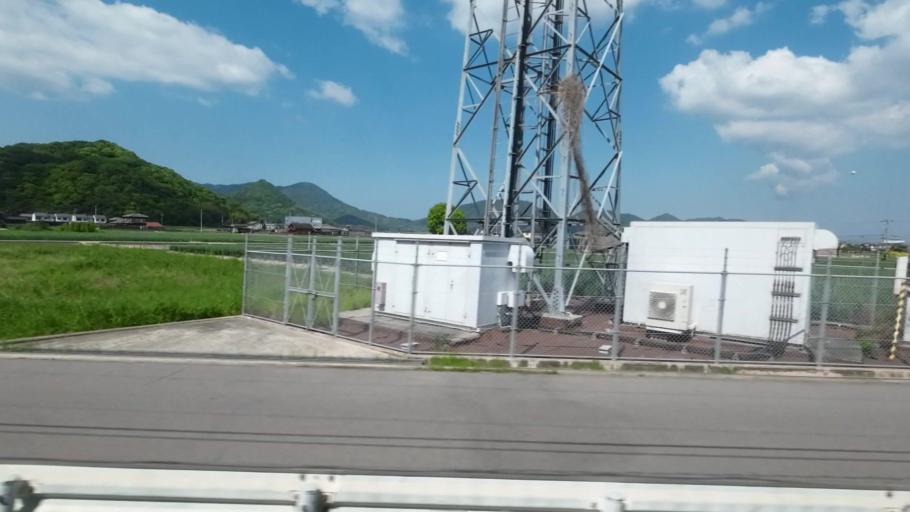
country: JP
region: Kagawa
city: Tadotsu
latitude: 34.1995
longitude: 133.7129
